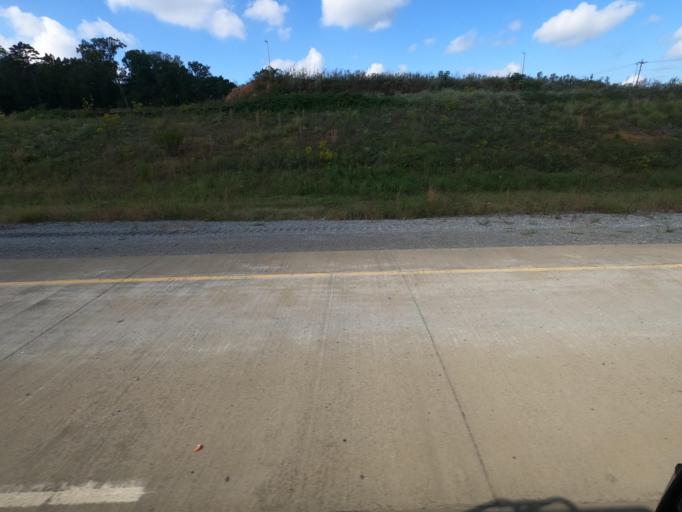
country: US
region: Tennessee
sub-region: Blount County
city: Alcoa
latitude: 35.7967
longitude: -83.9901
